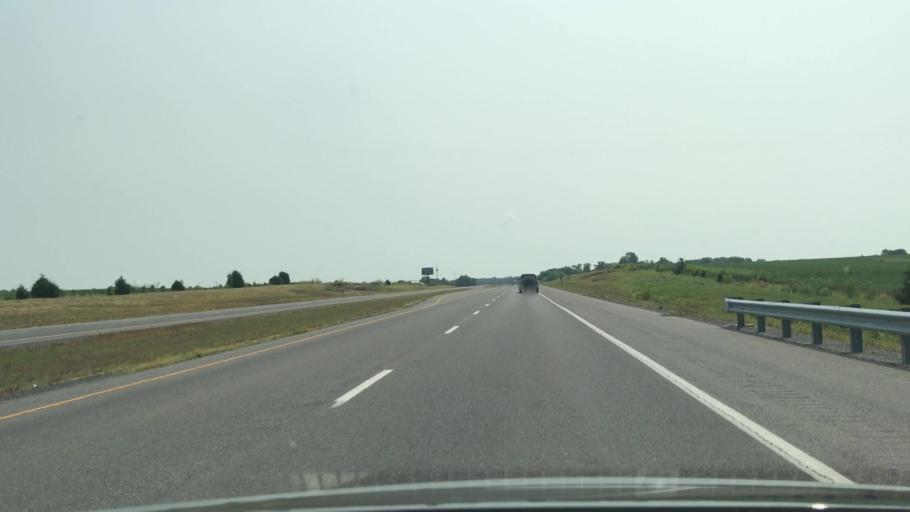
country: US
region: Kentucky
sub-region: Calloway County
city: Murray
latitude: 36.6500
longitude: -88.2602
